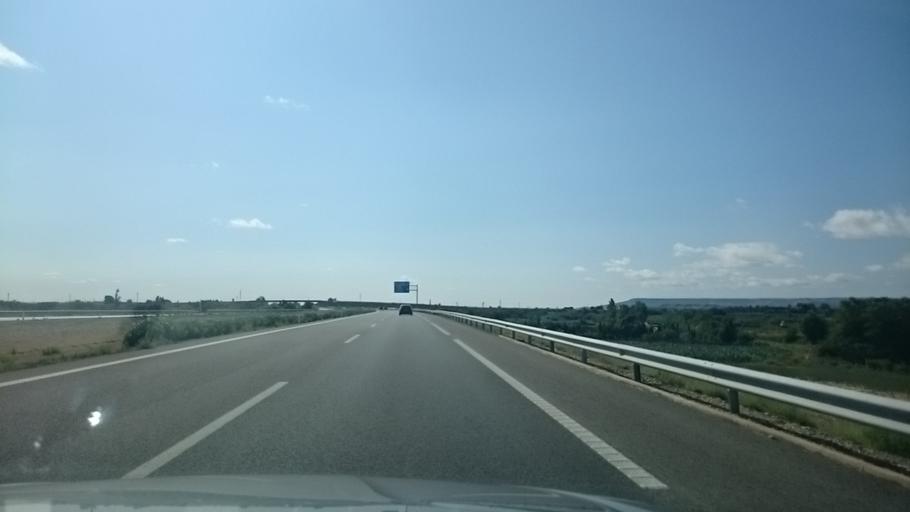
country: ES
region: Navarre
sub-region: Provincia de Navarra
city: Murchante
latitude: 42.0371
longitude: -1.6456
